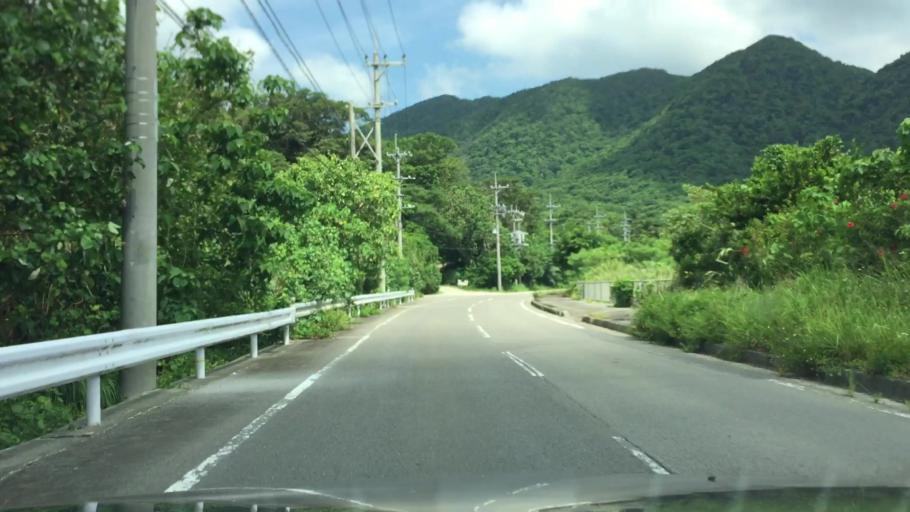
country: JP
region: Okinawa
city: Ishigaki
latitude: 24.4540
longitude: 124.2103
